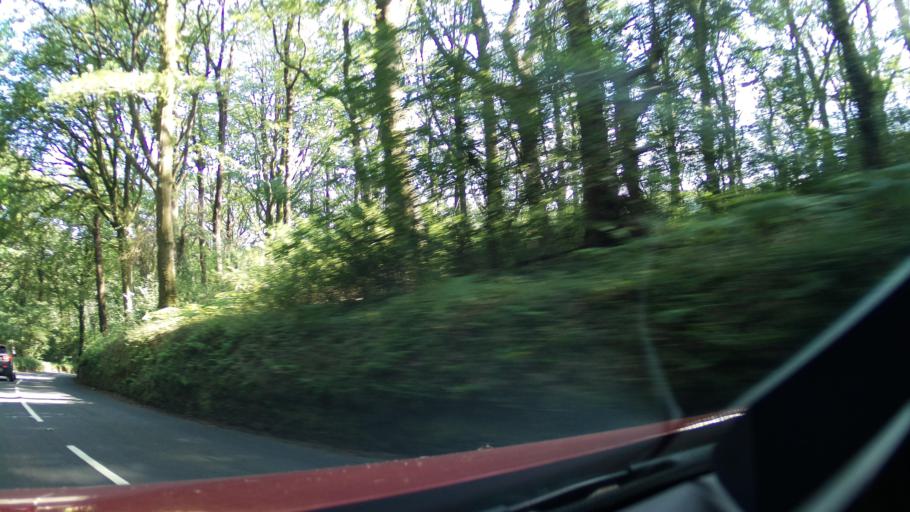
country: GB
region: England
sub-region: Devon
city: Buckfastleigh
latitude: 50.5224
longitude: -3.8070
